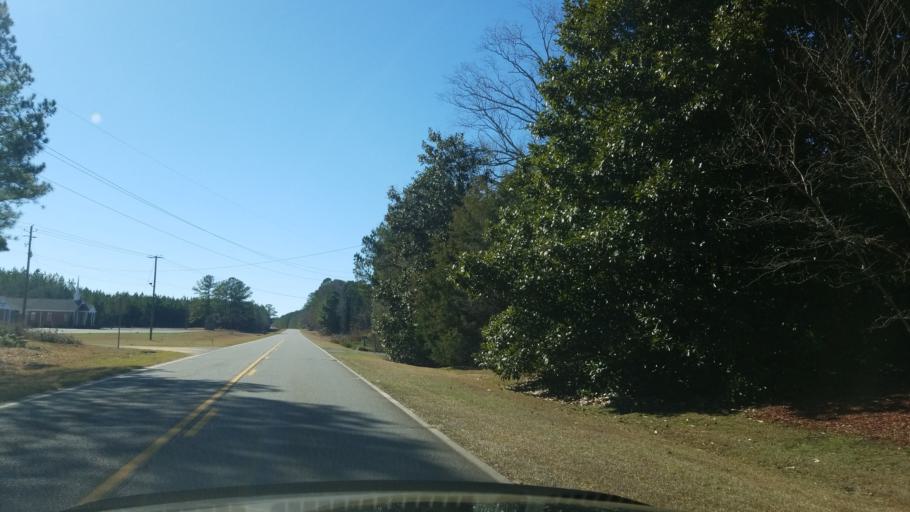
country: US
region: Georgia
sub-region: Talbot County
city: Sardis
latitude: 32.8061
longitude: -84.6539
